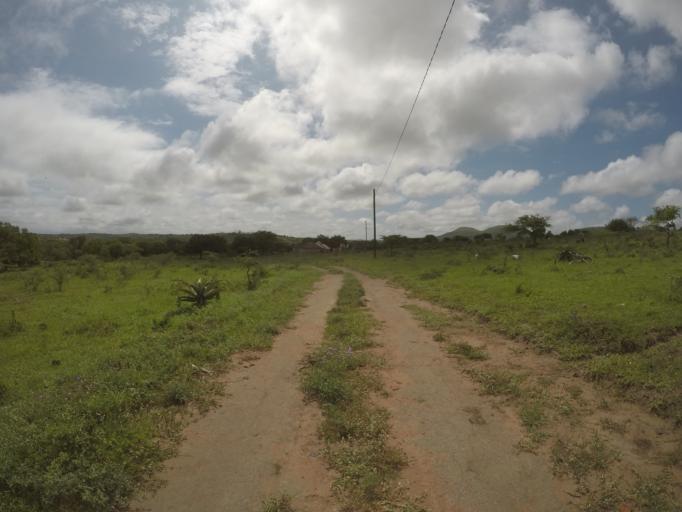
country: ZA
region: KwaZulu-Natal
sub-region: uThungulu District Municipality
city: Empangeni
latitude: -28.5714
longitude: 31.8443
